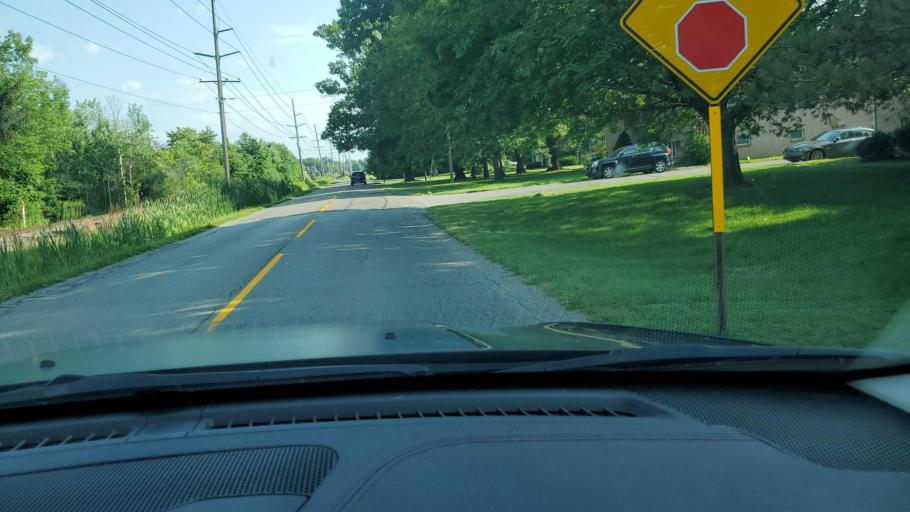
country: US
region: Ohio
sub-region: Mahoning County
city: Boardman
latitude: 40.9990
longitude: -80.6532
